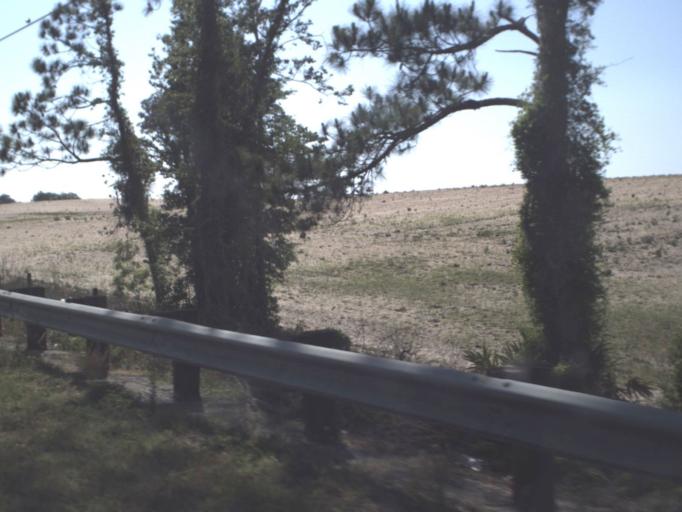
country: US
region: Florida
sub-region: Marion County
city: Dunnellon
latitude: 29.1235
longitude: -82.4278
